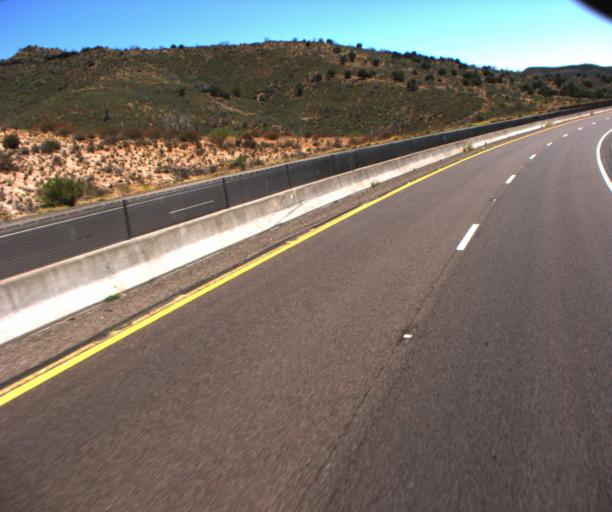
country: US
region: Arizona
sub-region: Gila County
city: Tonto Basin
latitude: 33.8821
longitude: -111.4535
